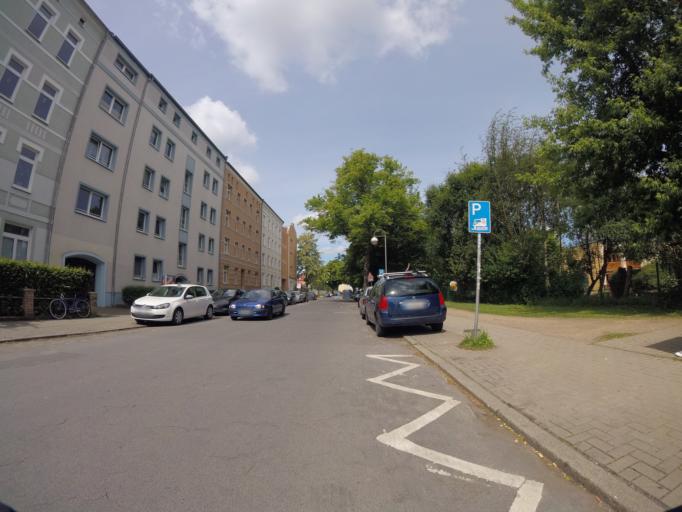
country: DE
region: Mecklenburg-Vorpommern
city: Rostock
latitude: 54.0897
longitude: 12.1079
